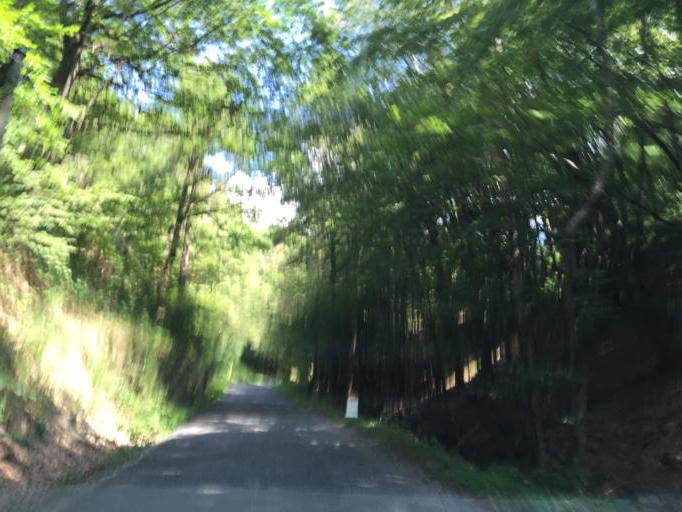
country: FR
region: Rhone-Alpes
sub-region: Departement de la Loire
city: Saint-Jean-Bonnefonds
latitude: 45.4203
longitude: 4.4503
